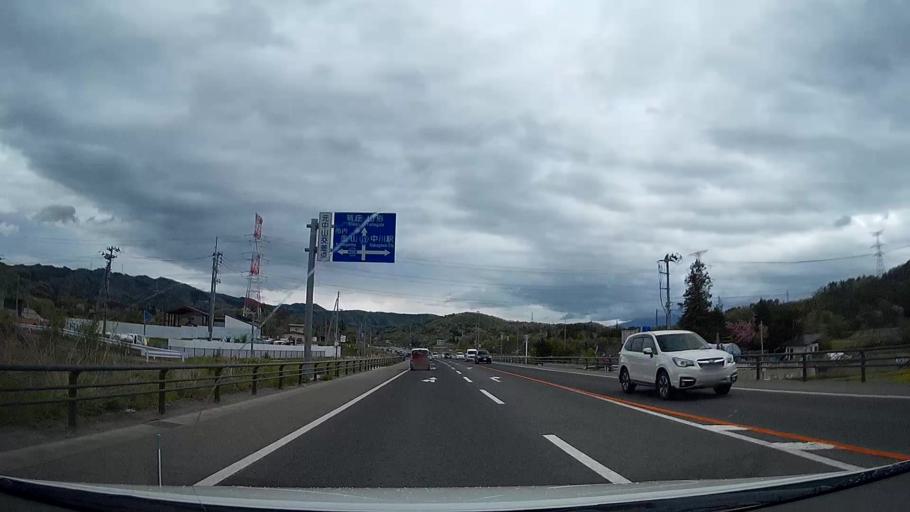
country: JP
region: Yamagata
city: Kaminoyama
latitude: 38.1038
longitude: 140.2079
